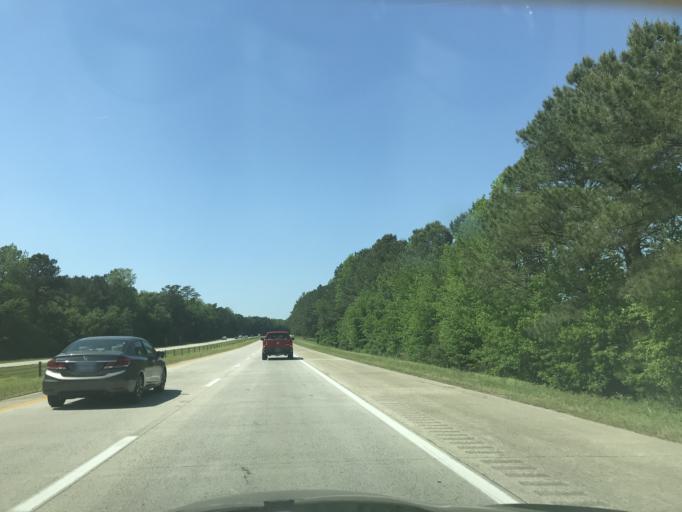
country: US
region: North Carolina
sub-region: Johnston County
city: Benson
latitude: 35.4637
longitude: -78.5436
